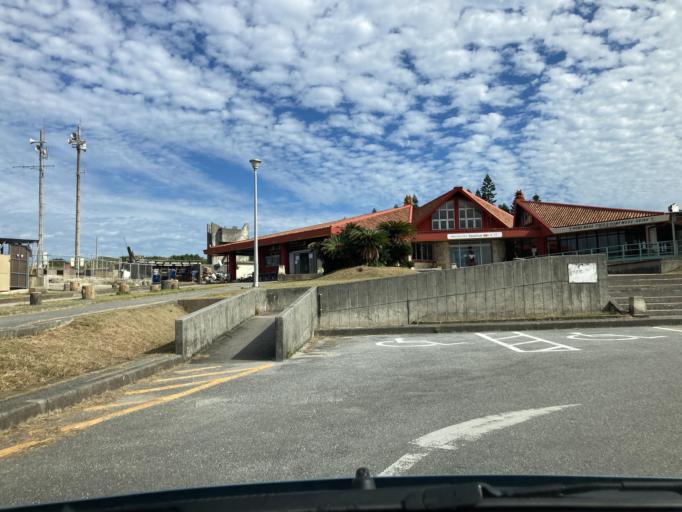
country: JP
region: Okinawa
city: Ishikawa
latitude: 26.4385
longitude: 127.7146
